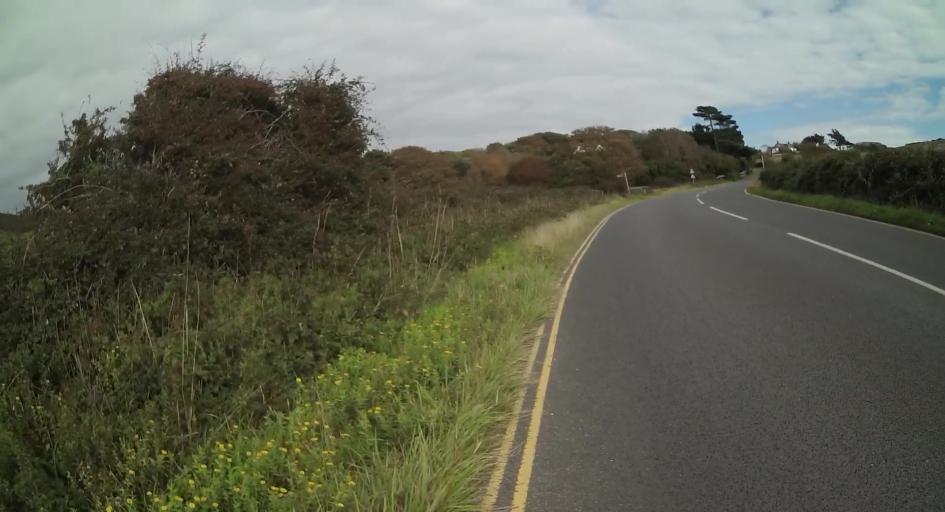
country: GB
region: England
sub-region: Isle of Wight
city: Totland
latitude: 50.6691
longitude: -1.5581
